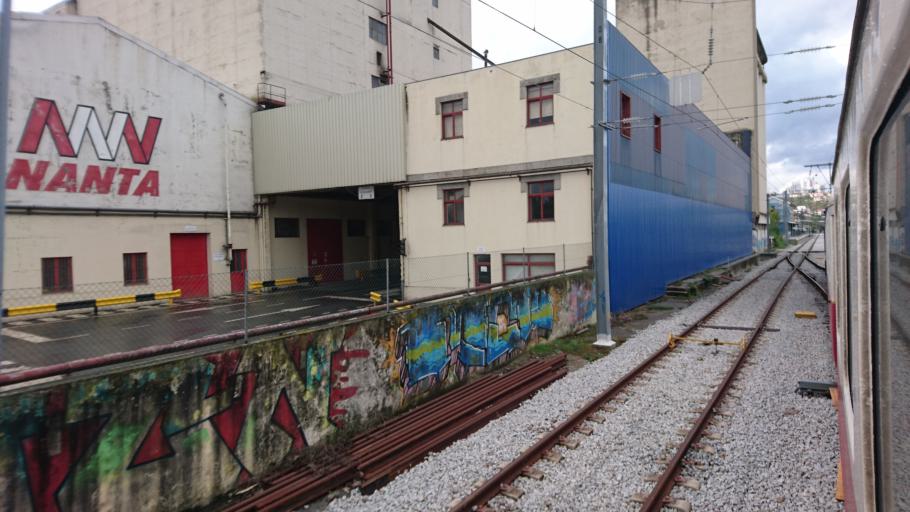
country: PT
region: Porto
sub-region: Marco de Canaveses
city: Marco de Canavezes
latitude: 41.1787
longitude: -8.1350
